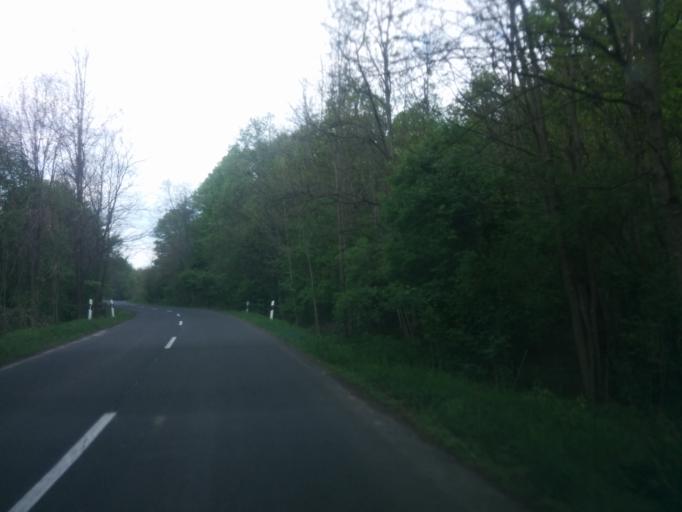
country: HU
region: Nograd
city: Romhany
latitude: 47.8865
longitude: 19.2298
